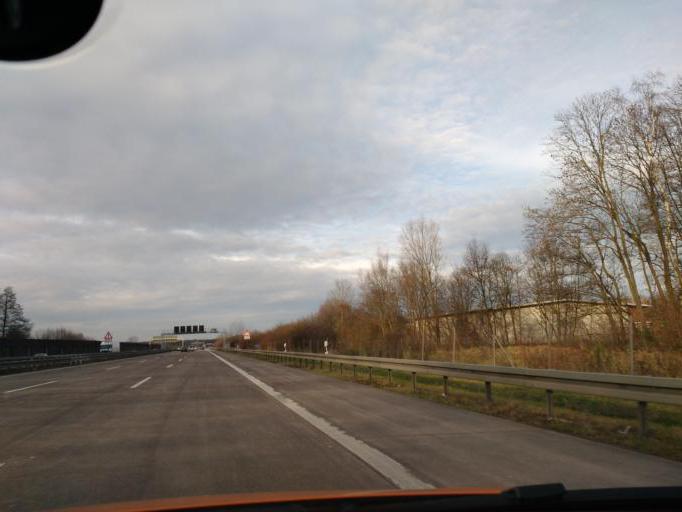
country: DE
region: Lower Saxony
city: Isernhagen Farster Bauerschaft
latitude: 52.4382
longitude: 9.8757
